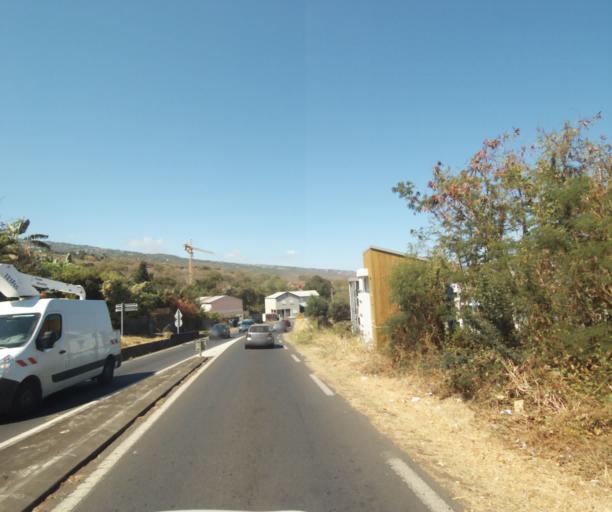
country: RE
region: Reunion
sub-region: Reunion
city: Le Port
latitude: -20.9801
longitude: 55.3177
